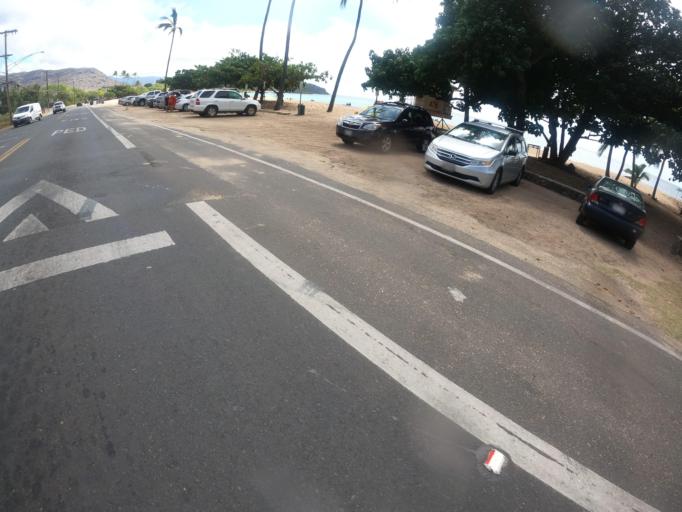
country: US
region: Hawaii
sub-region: Honolulu County
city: Makaha
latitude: 21.4787
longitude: -158.2228
